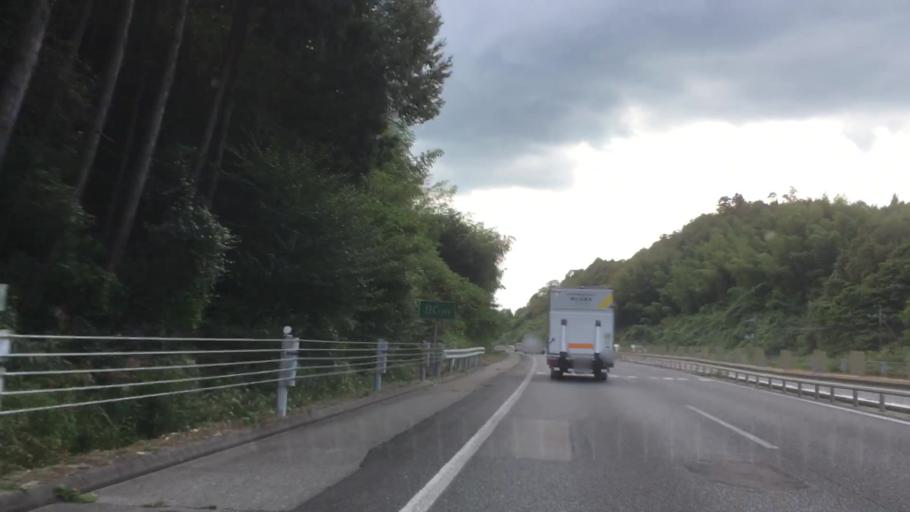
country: JP
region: Yamaguchi
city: Iwakuni
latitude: 34.1324
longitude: 132.1134
